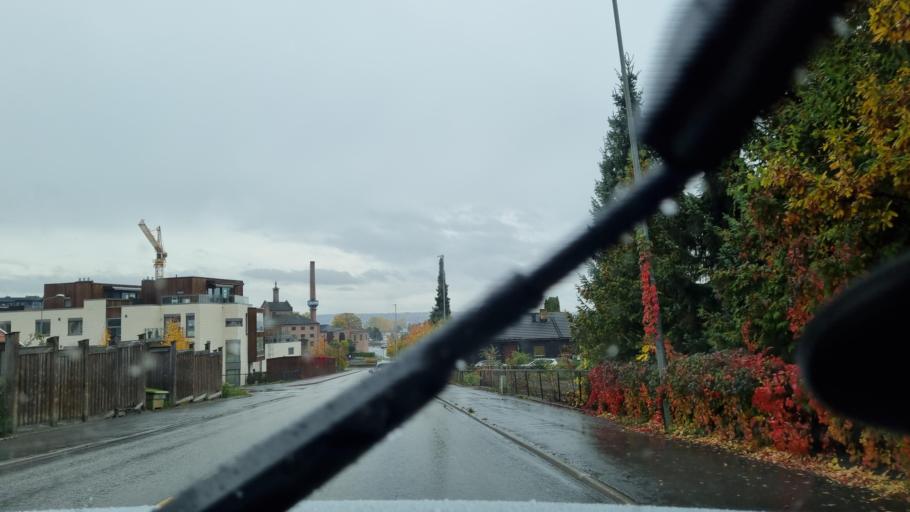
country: NO
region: Hedmark
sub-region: Hamar
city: Hamar
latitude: 60.7960
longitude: 11.0557
